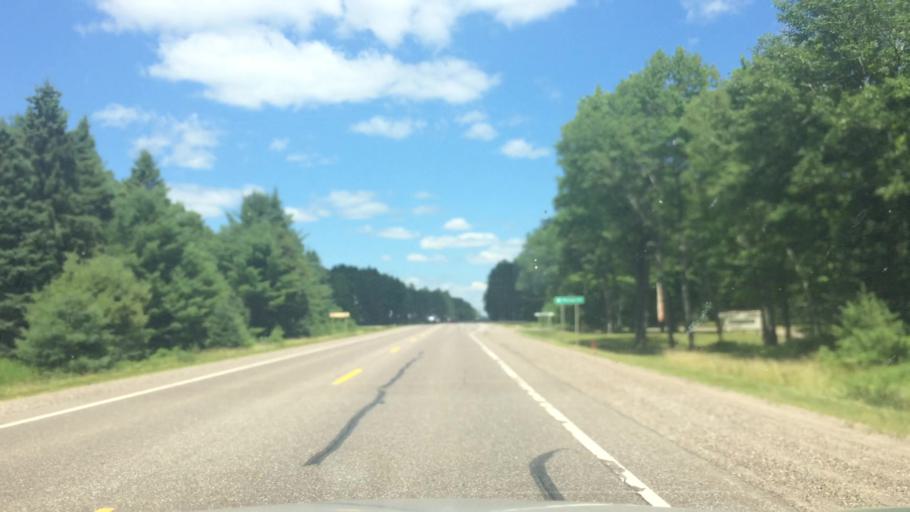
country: US
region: Wisconsin
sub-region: Vilas County
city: Lac du Flambeau
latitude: 45.9802
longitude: -89.6989
